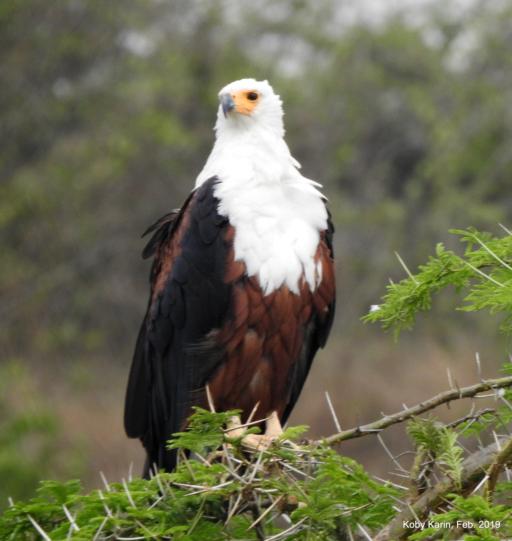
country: UG
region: Western Region
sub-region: Rubirizi District
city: Rubirizi
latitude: -0.1963
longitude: 29.9097
